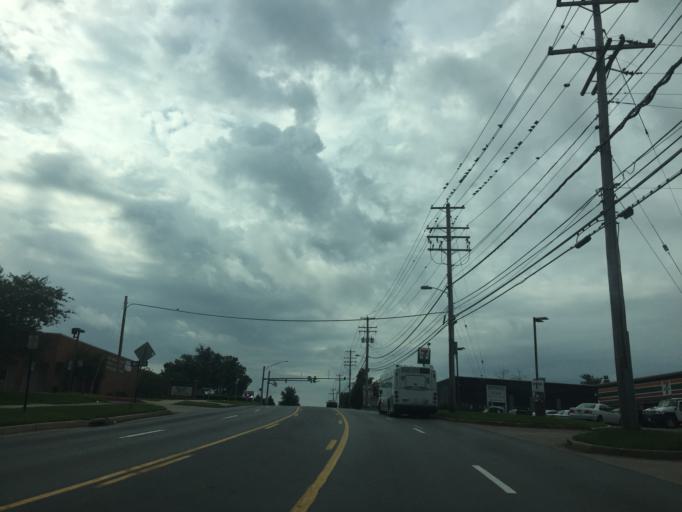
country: US
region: Maryland
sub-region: Baltimore County
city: Woodlawn
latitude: 39.3172
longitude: -76.7374
